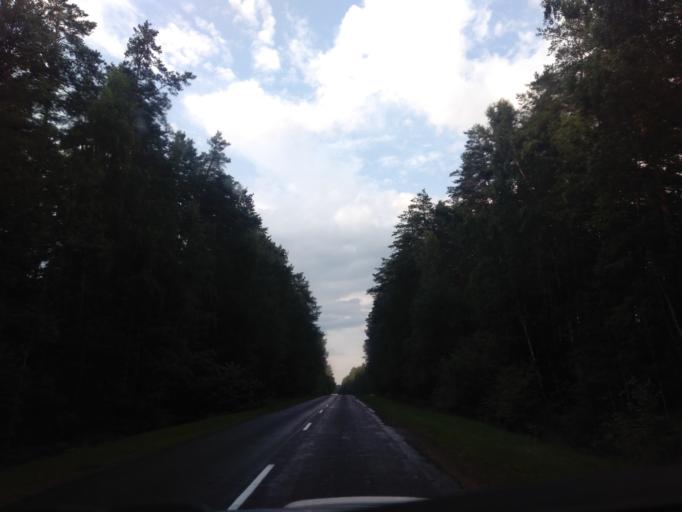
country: BY
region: Minsk
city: Uzda
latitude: 53.3708
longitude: 27.1039
